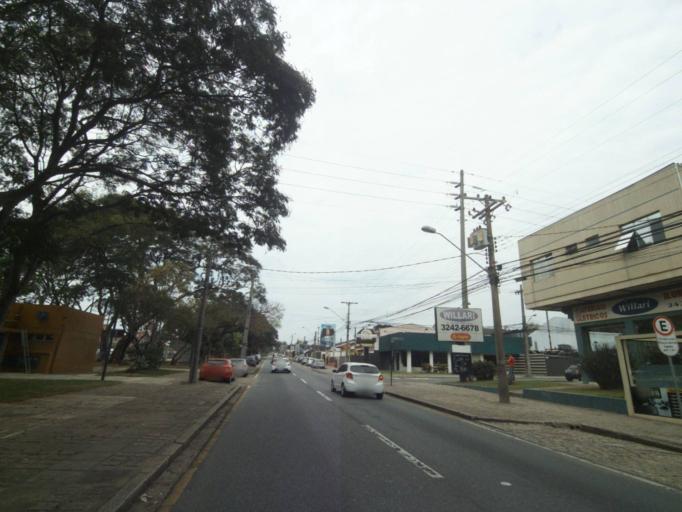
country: BR
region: Parana
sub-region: Curitiba
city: Curitiba
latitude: -25.4576
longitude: -49.3030
